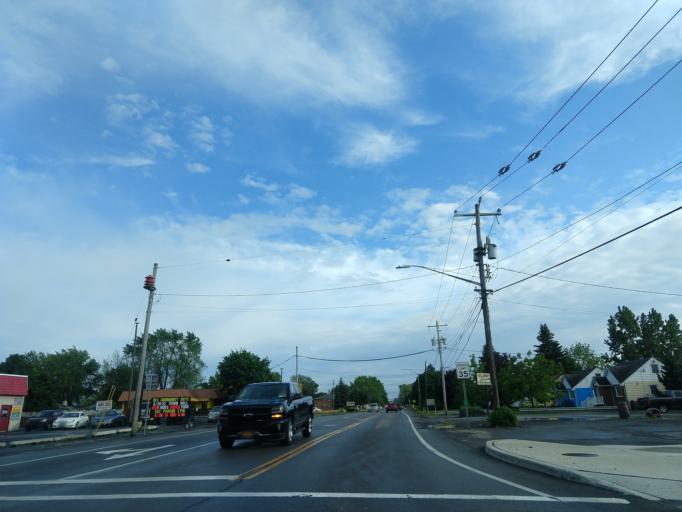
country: US
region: New York
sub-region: Erie County
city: West Seneca
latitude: 42.8644
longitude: -78.7873
